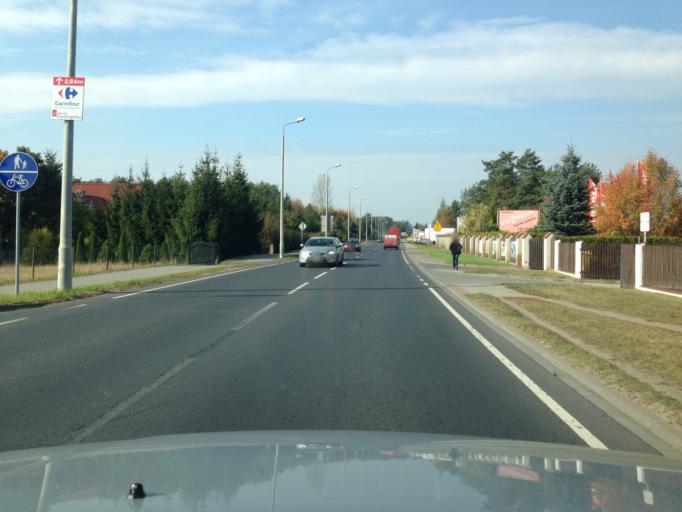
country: PL
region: Kujawsko-Pomorskie
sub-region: Grudziadz
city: Grudziadz
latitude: 53.4547
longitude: 18.7906
